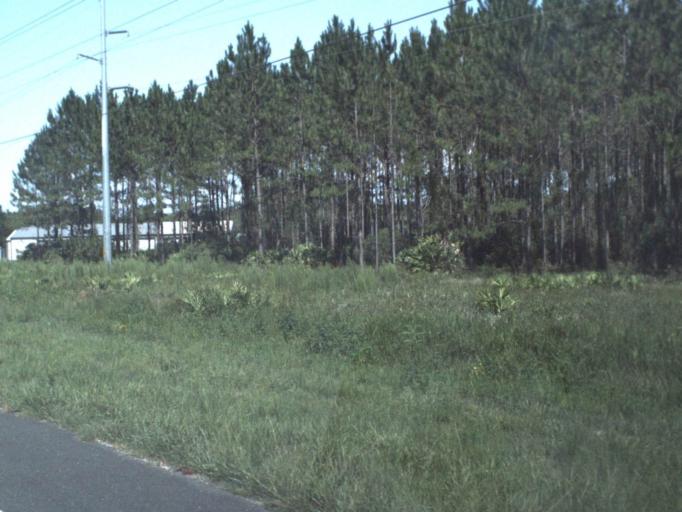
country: US
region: Florida
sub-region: Levy County
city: Chiefland
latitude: 29.2302
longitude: -82.9473
